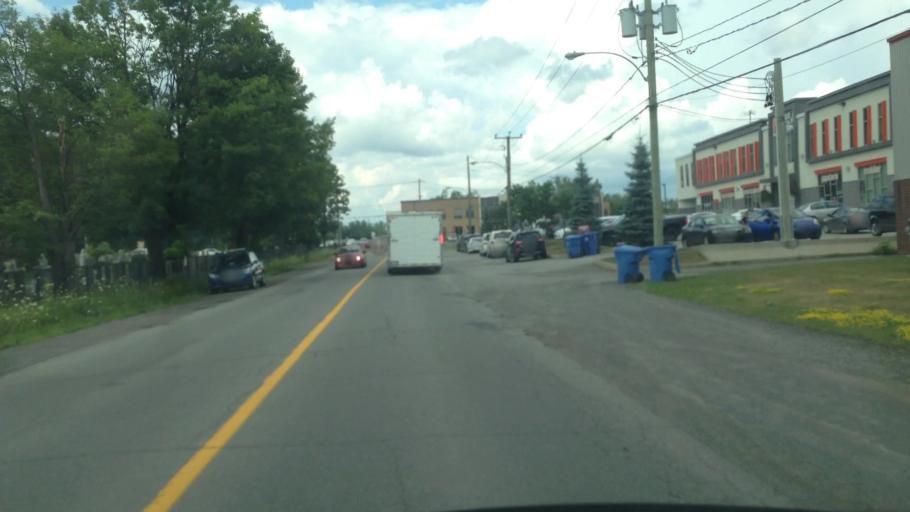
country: CA
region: Quebec
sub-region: Laurentides
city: Saint-Jerome
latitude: 45.7775
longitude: -74.0239
